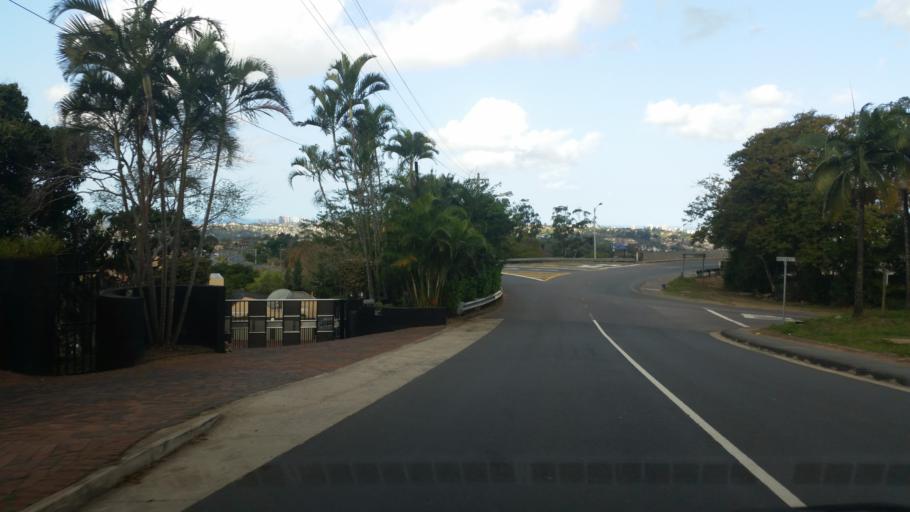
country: ZA
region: KwaZulu-Natal
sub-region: eThekwini Metropolitan Municipality
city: Berea
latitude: -29.8313
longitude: 30.9400
